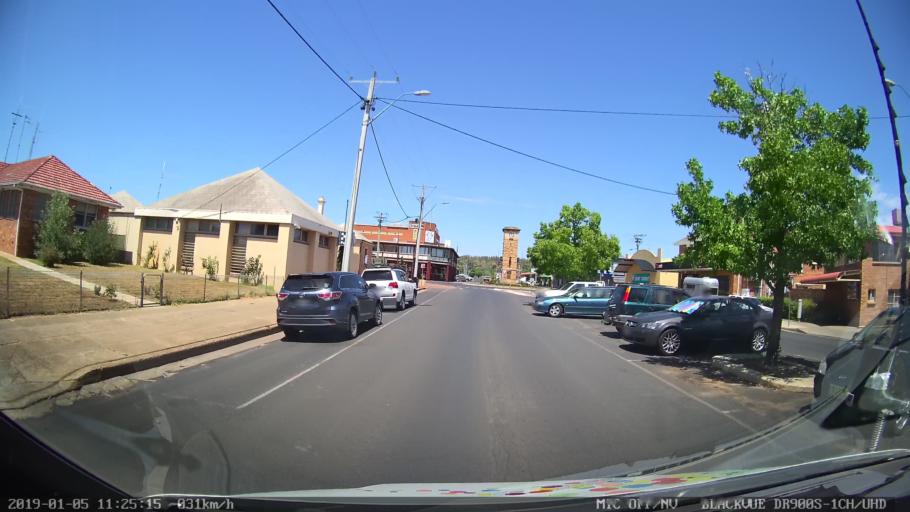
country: AU
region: New South Wales
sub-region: Warrumbungle Shire
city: Coonabarabran
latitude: -31.2732
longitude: 149.2781
